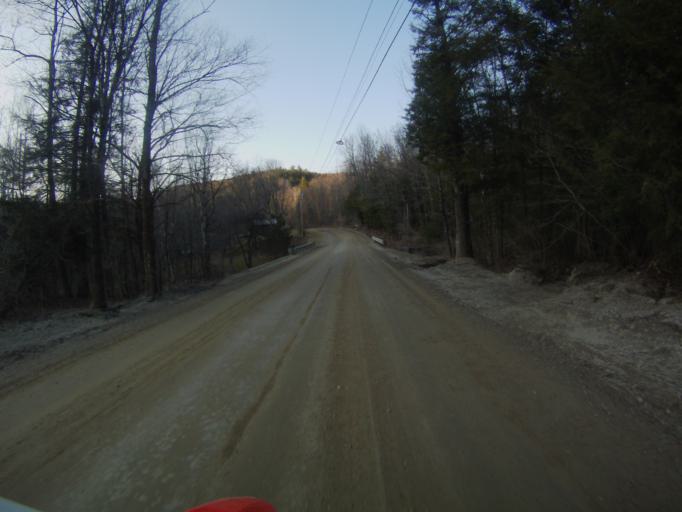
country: US
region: Vermont
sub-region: Addison County
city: Bristol
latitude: 44.0741
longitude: -73.0603
